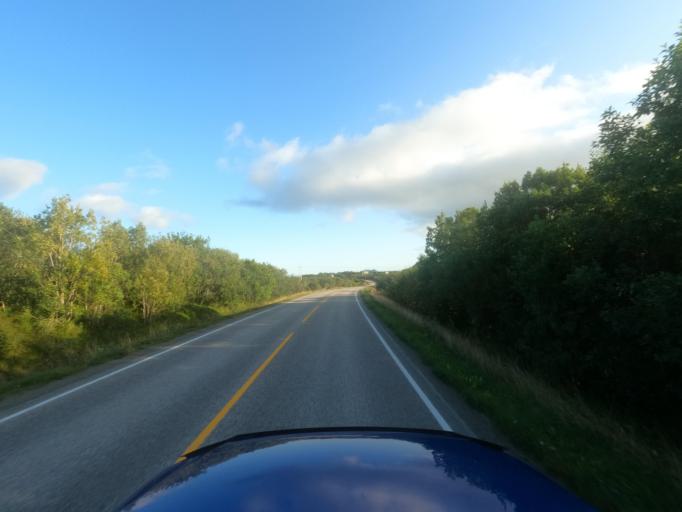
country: NO
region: Nordland
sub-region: Vestvagoy
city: Gravdal
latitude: 68.1484
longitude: 13.5456
